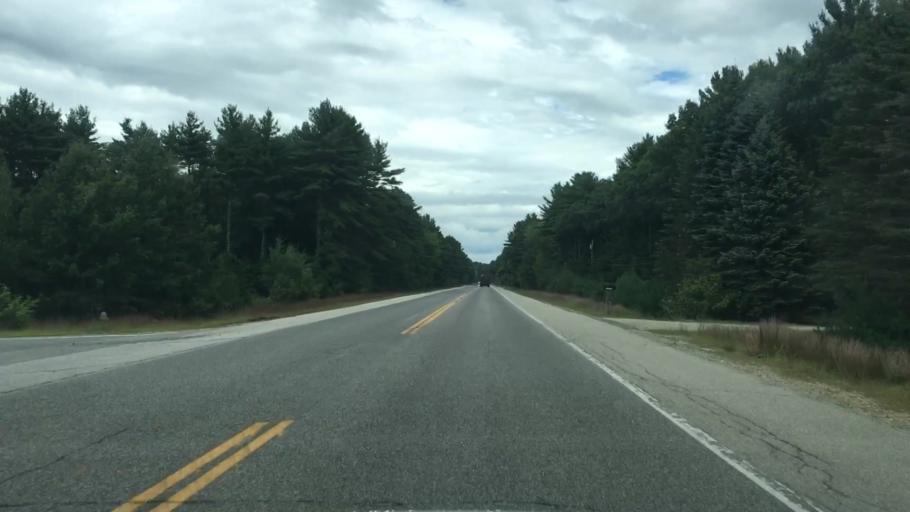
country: US
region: Maine
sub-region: York County
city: North Berwick
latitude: 43.3440
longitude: -70.7311
